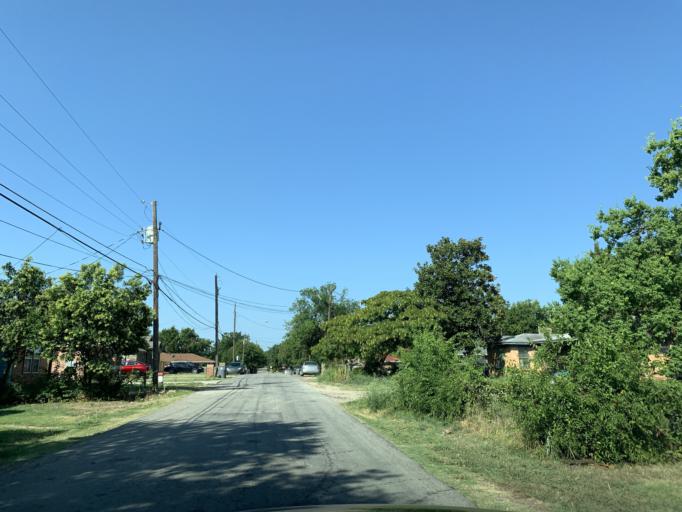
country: US
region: Texas
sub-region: Dallas County
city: Hutchins
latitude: 32.6674
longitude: -96.7568
